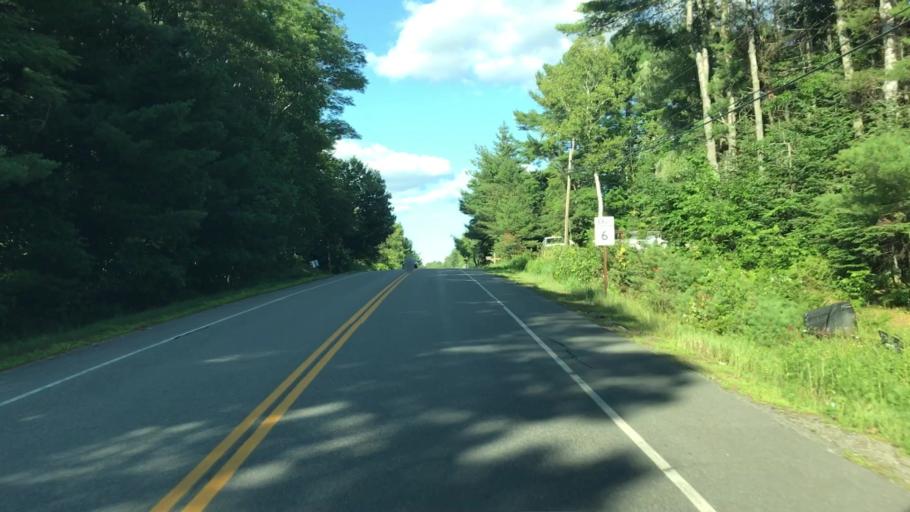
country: US
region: Maine
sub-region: Penobscot County
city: Lincoln
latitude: 45.3770
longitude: -68.4607
